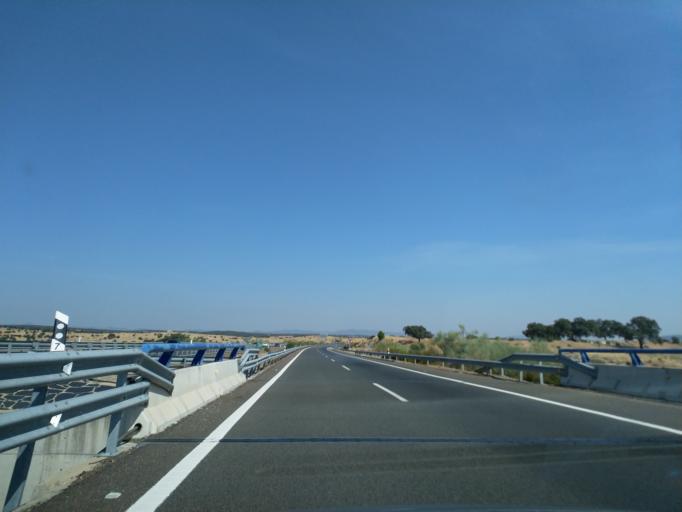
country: ES
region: Extremadura
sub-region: Provincia de Badajoz
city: Mirandilla
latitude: 38.9769
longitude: -6.3343
